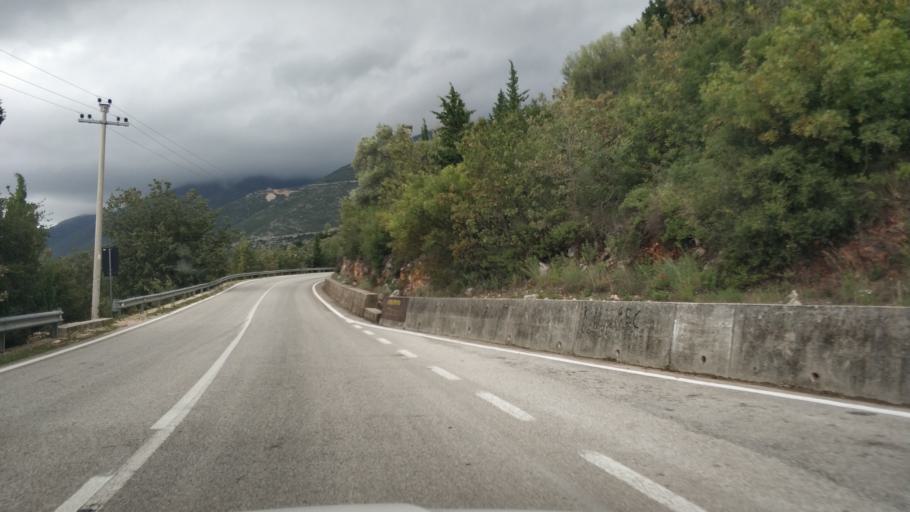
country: AL
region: Vlore
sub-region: Rrethi i Vlores
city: Vranisht
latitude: 40.1679
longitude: 19.6188
